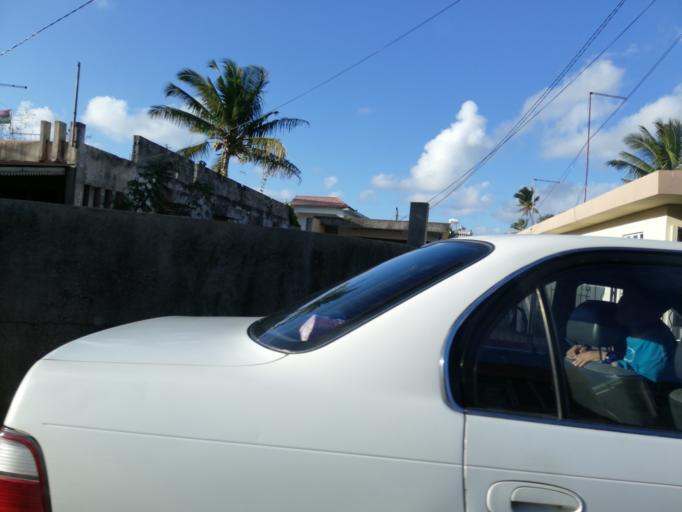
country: MU
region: Pamplemousses
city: Triolet
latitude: -20.0456
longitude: 57.5546
